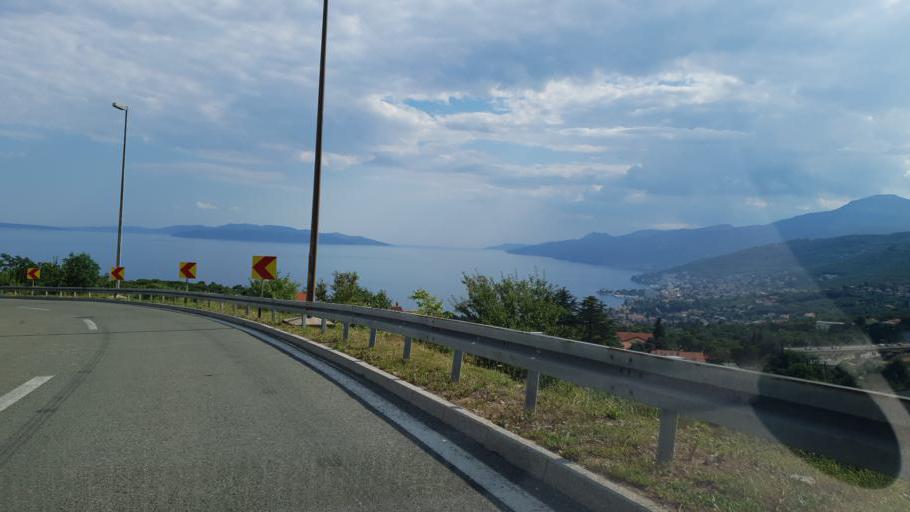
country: HR
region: Primorsko-Goranska
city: Matulji
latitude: 45.3642
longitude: 14.3313
